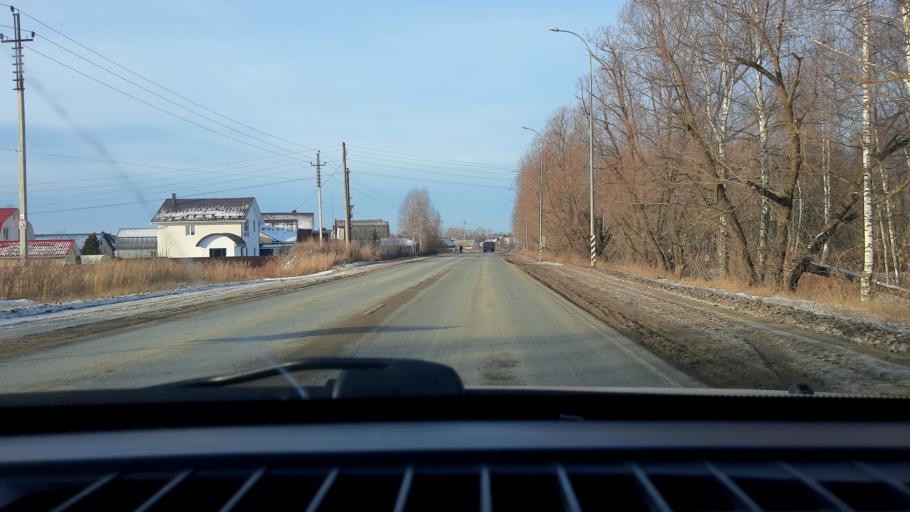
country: RU
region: Nizjnij Novgorod
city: Bor
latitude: 56.3788
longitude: 44.0472
